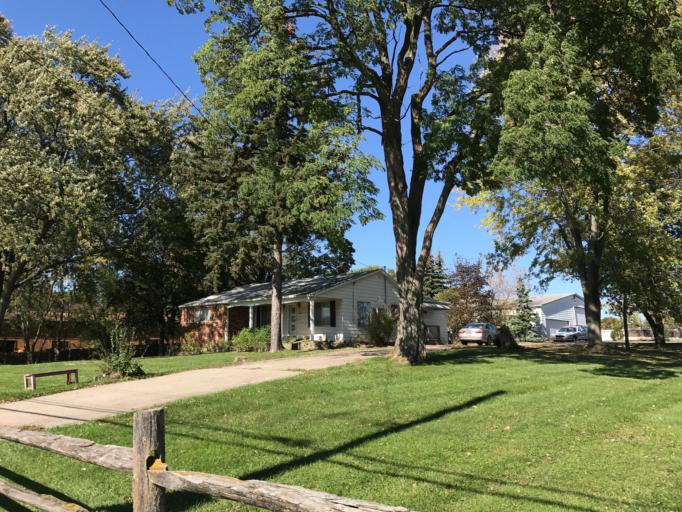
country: US
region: Michigan
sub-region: Oakland County
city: Franklin
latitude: 42.5006
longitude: -83.3127
